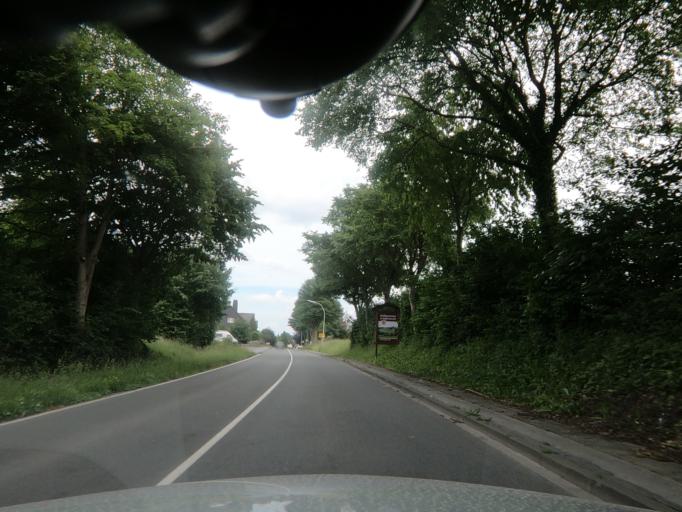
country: DE
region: North Rhine-Westphalia
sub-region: Regierungsbezirk Arnsberg
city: Ruthen
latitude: 51.4519
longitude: 8.4186
